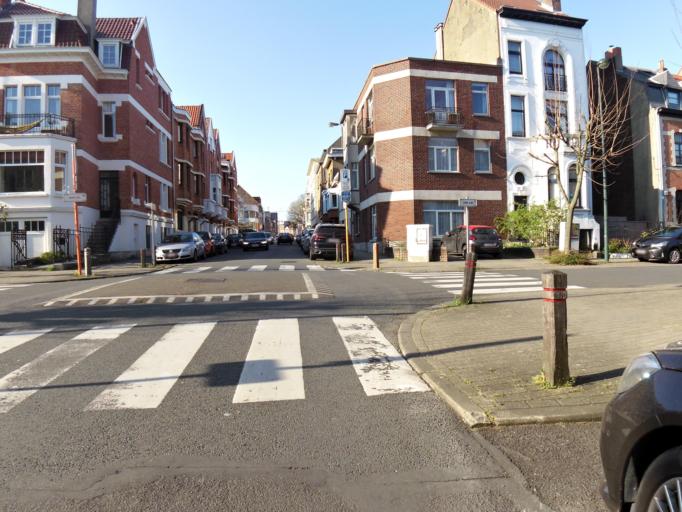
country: BE
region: Flanders
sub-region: Provincie Vlaams-Brabant
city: Diegem
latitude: 50.8448
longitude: 4.4096
